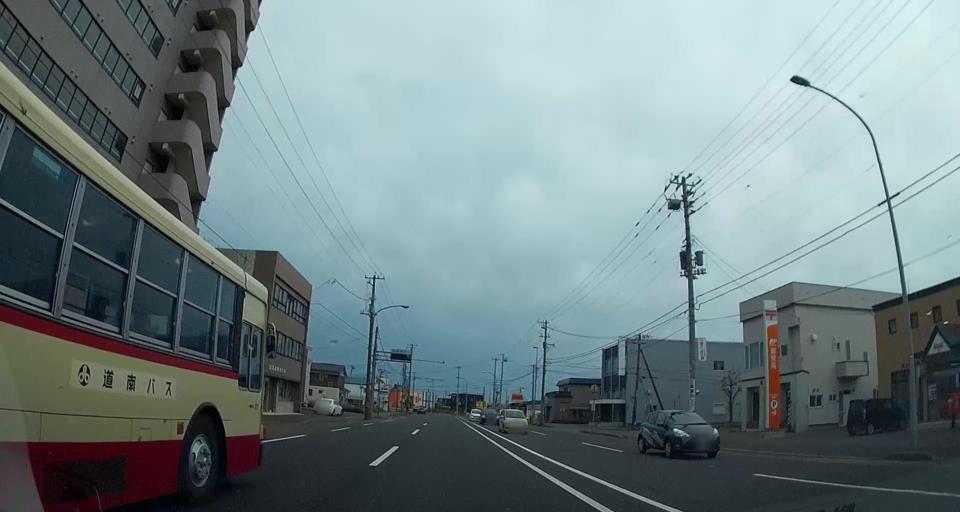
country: JP
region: Hokkaido
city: Tomakomai
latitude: 42.6287
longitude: 141.5942
